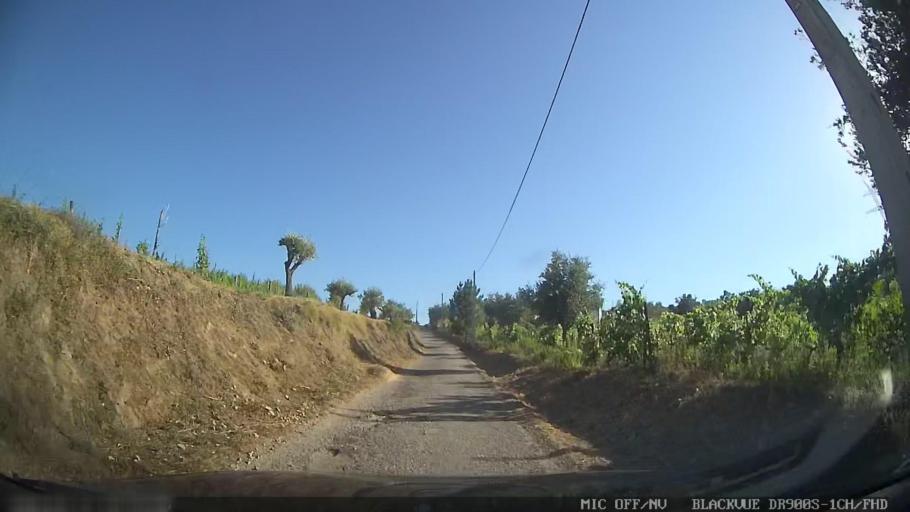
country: PT
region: Viseu
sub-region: Sao Joao da Pesqueira
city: Sao Joao da Pesqueira
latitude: 41.1556
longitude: -7.4201
